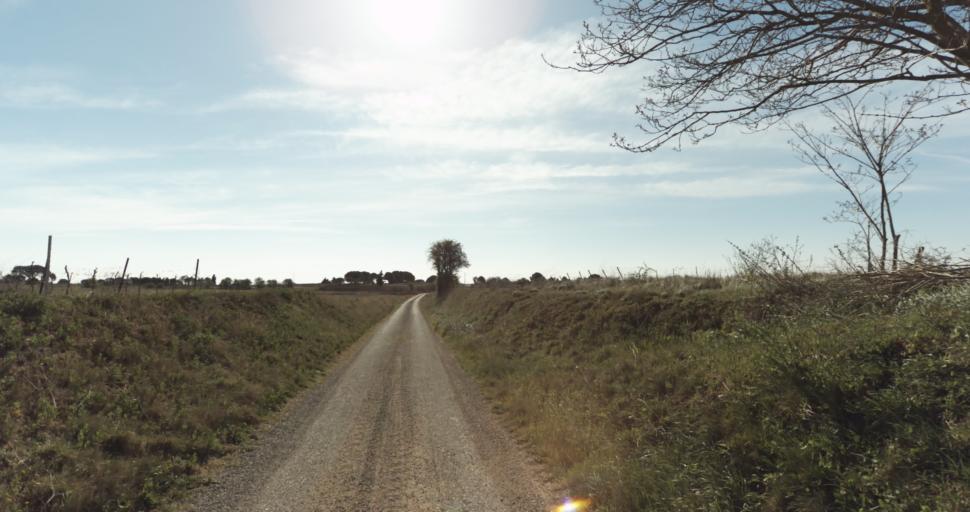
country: FR
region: Languedoc-Roussillon
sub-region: Departement de l'Herault
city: Marseillan
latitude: 43.3479
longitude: 3.5041
